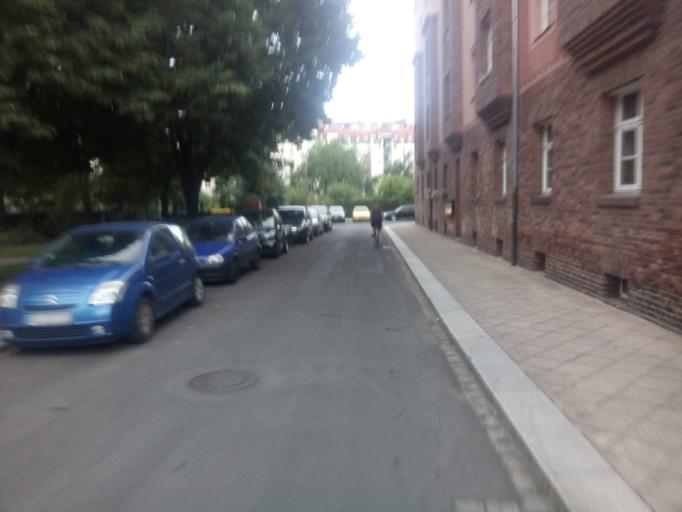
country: DE
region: Saxony
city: Albertstadt
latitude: 51.0491
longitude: 13.7795
